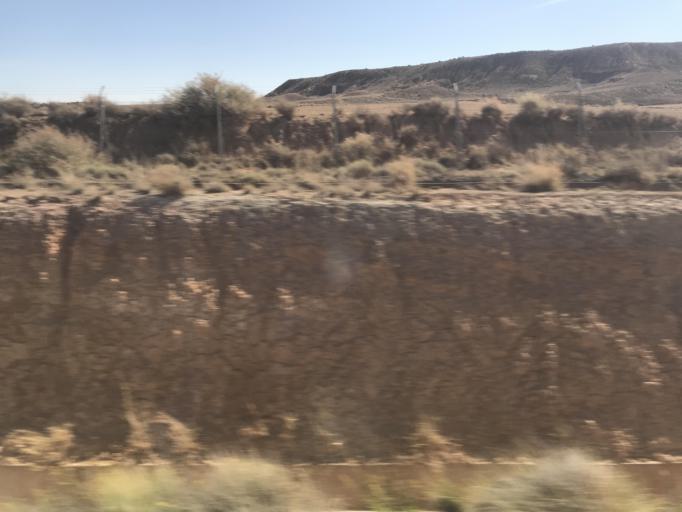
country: ES
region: Aragon
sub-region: Provincia de Huesca
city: Candasnos
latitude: 41.5655
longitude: 0.0906
